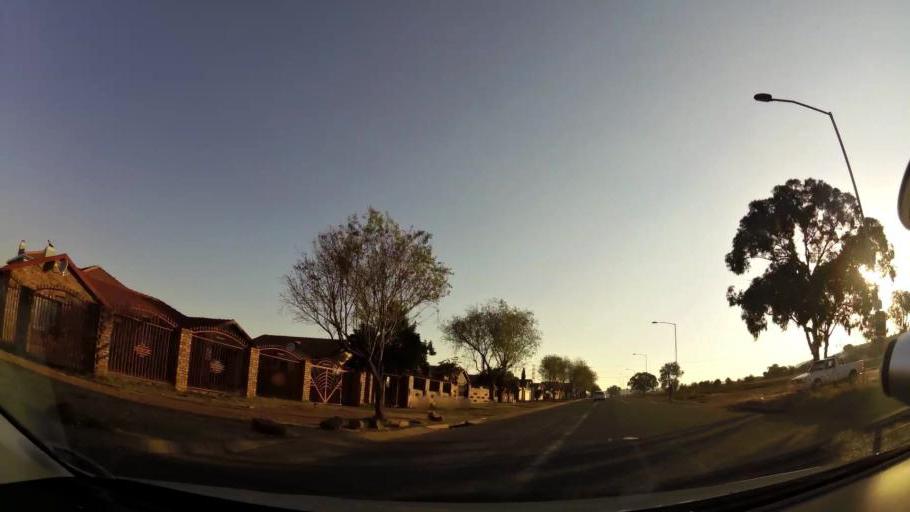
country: ZA
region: Gauteng
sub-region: City of Tshwane Metropolitan Municipality
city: Pretoria
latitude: -25.7447
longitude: 28.1097
